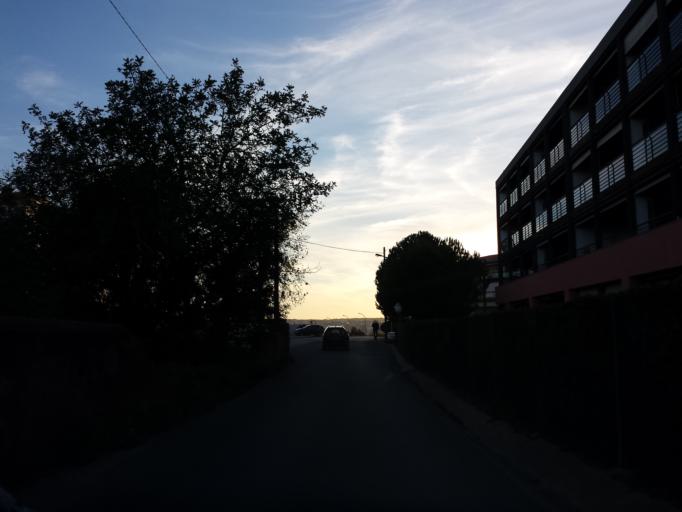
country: PT
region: Faro
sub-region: Lagos
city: Lagos
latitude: 37.1156
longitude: -8.6693
